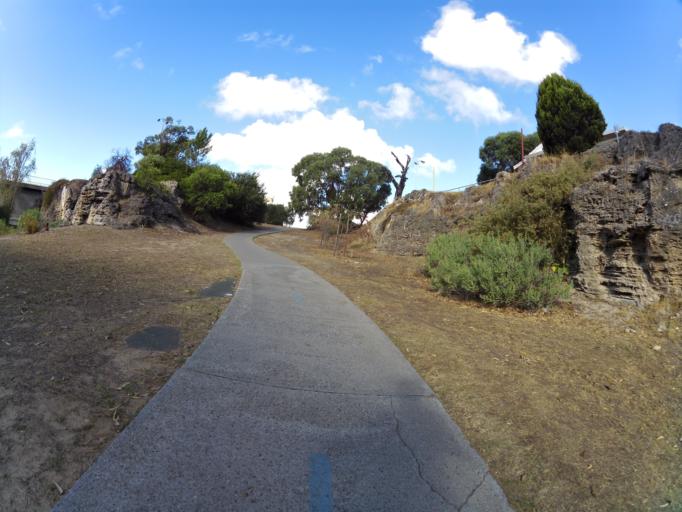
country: AU
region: Western Australia
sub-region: East Fremantle
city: East Fremantle
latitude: -32.0410
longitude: 115.7606
